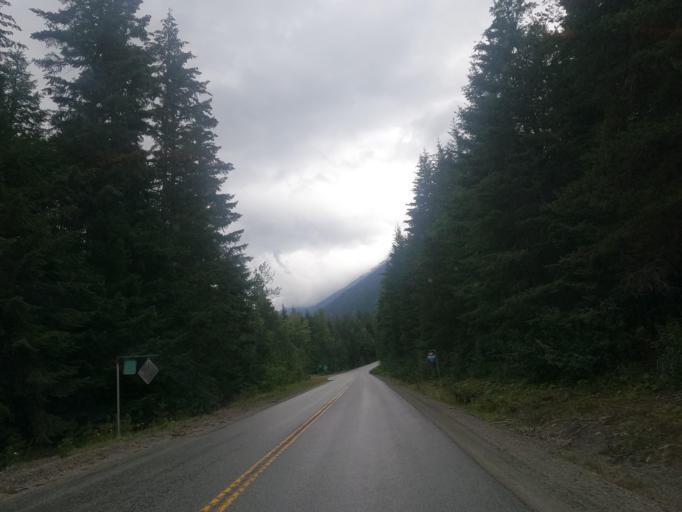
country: CA
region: British Columbia
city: Pemberton
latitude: 50.3080
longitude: -122.5779
